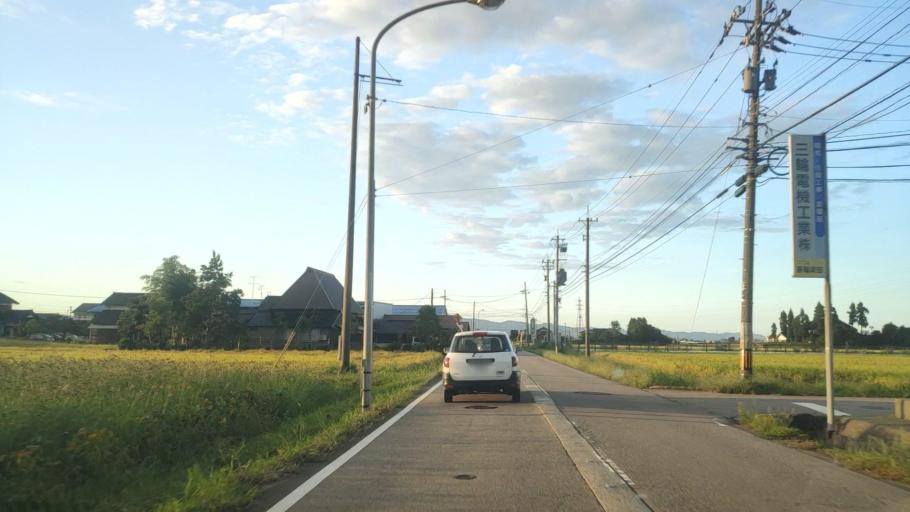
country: JP
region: Toyama
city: Nanto-shi
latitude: 36.6153
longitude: 136.8897
